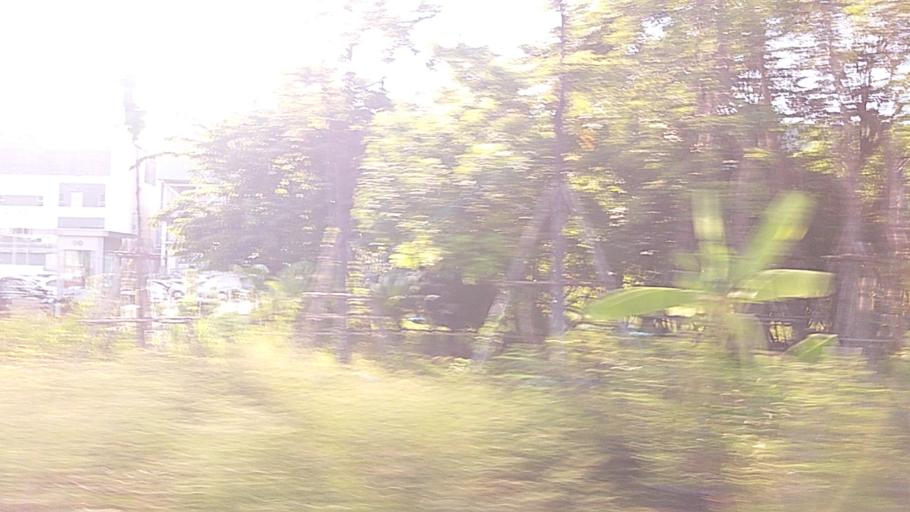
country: TH
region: Phra Nakhon Si Ayutthaya
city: Ban Bang Kadi Pathum Thani
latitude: 13.9882
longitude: 100.6203
